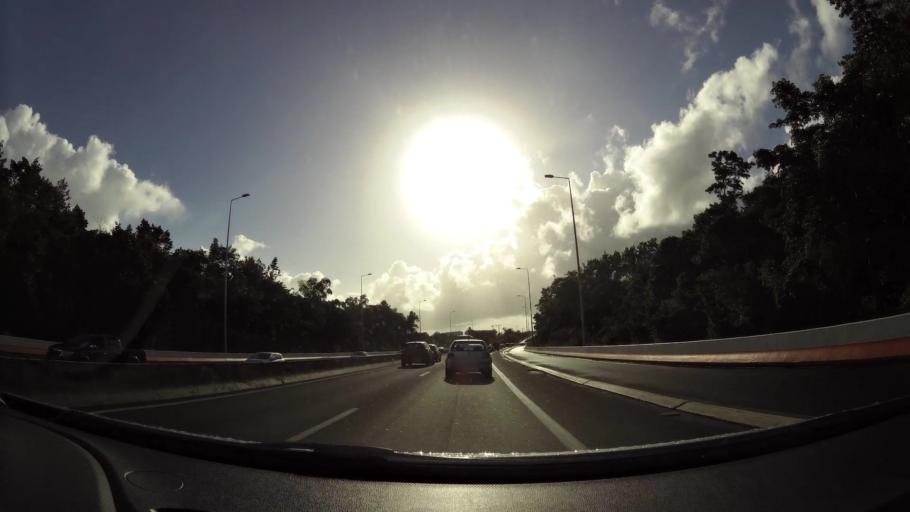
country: MQ
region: Martinique
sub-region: Martinique
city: Le Lamentin
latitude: 14.6125
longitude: -61.0088
